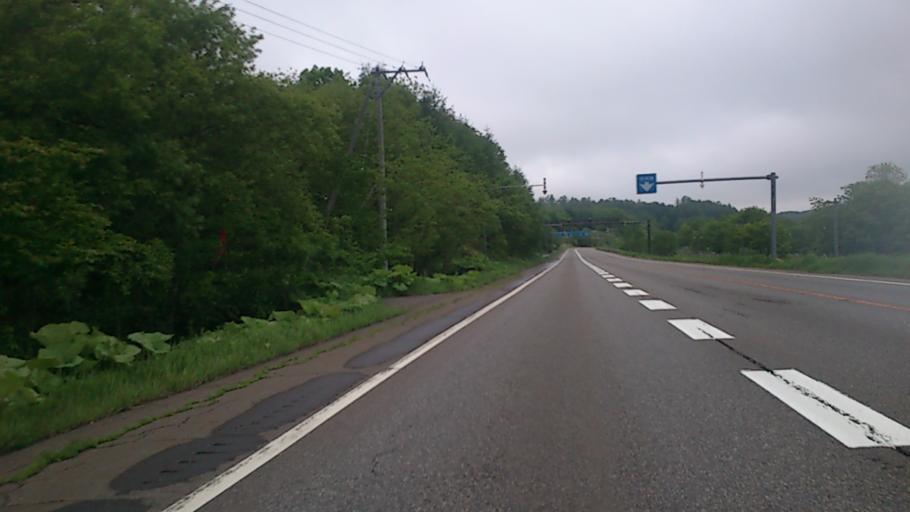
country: JP
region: Hokkaido
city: Obihiro
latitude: 42.8321
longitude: 143.7592
